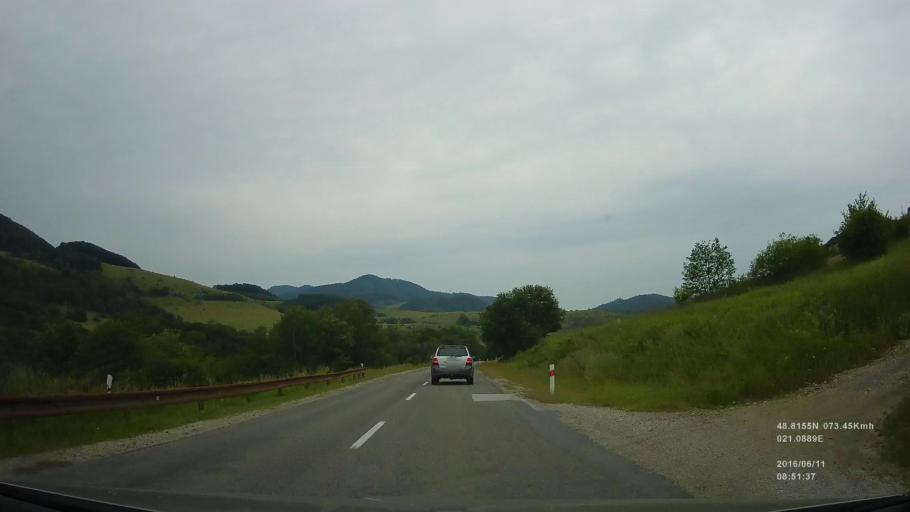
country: SK
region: Kosicky
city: Gelnica
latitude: 48.8106
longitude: 21.0961
